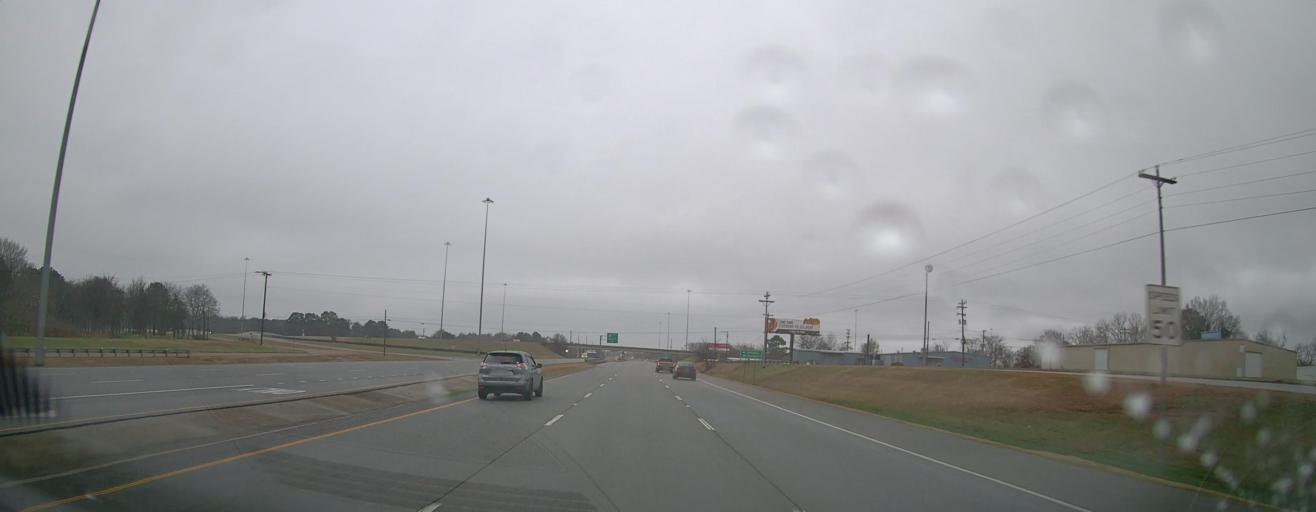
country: US
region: Alabama
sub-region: Morgan County
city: Decatur
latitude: 34.6059
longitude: -87.0313
